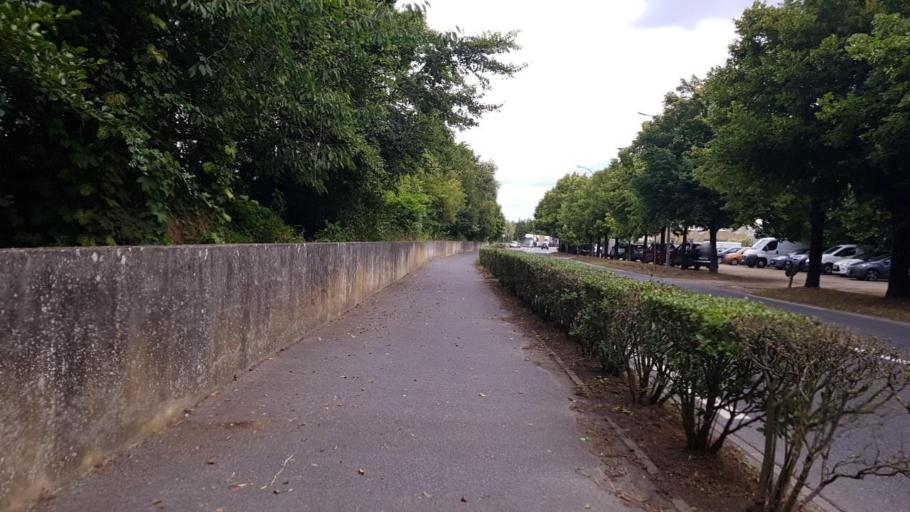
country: FR
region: Picardie
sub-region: Departement de l'Oise
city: Clairoix
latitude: 49.4305
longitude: 2.8392
